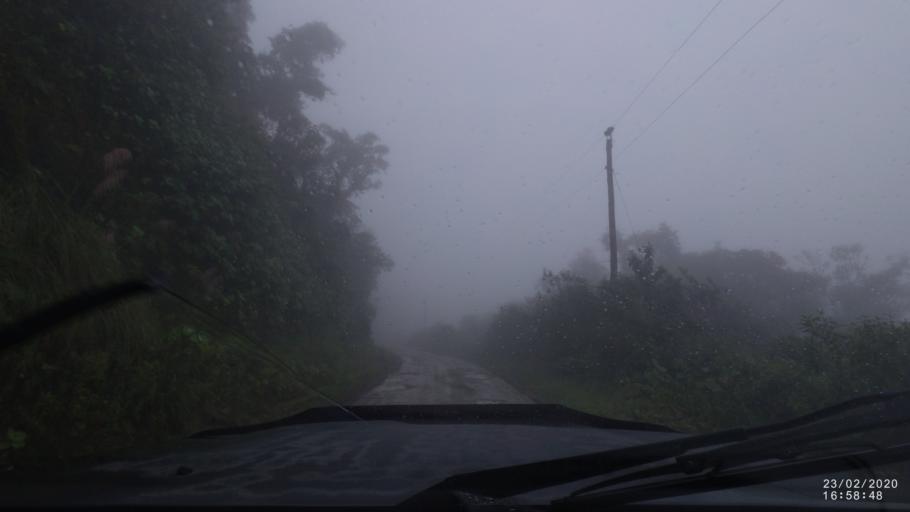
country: BO
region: Cochabamba
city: Colomi
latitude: -17.1068
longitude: -65.9736
